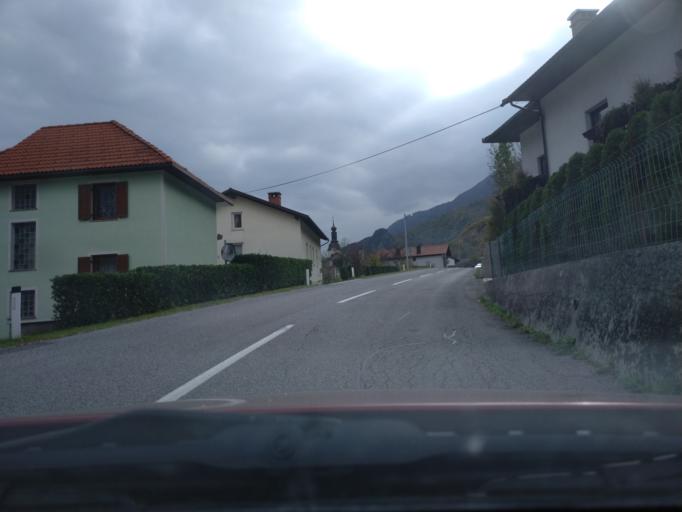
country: SI
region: Bovec
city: Bovec
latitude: 46.2924
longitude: 13.4971
